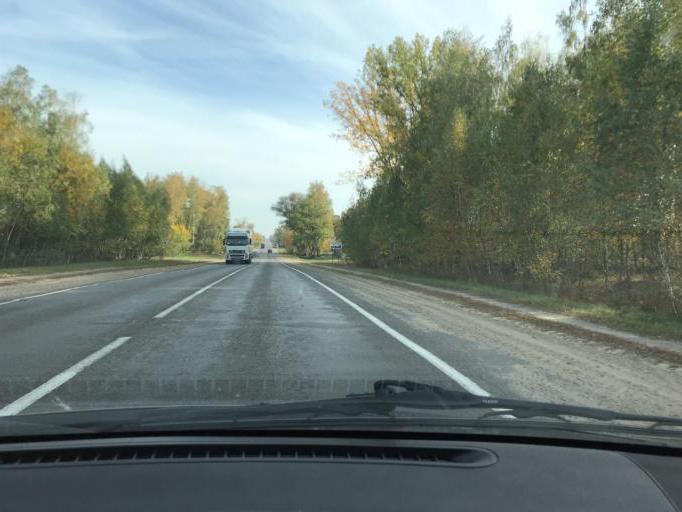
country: BY
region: Brest
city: Lahishyn
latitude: 52.2299
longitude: 26.0191
